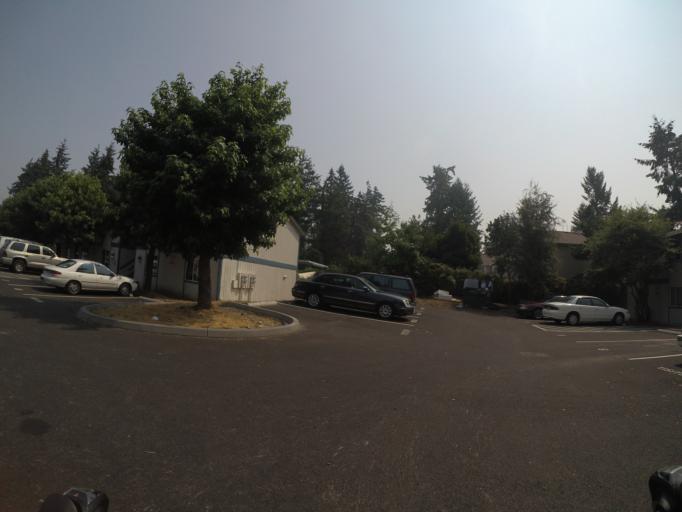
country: US
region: Washington
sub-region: Pierce County
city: McChord Air Force Base
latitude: 47.1428
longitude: -122.5108
